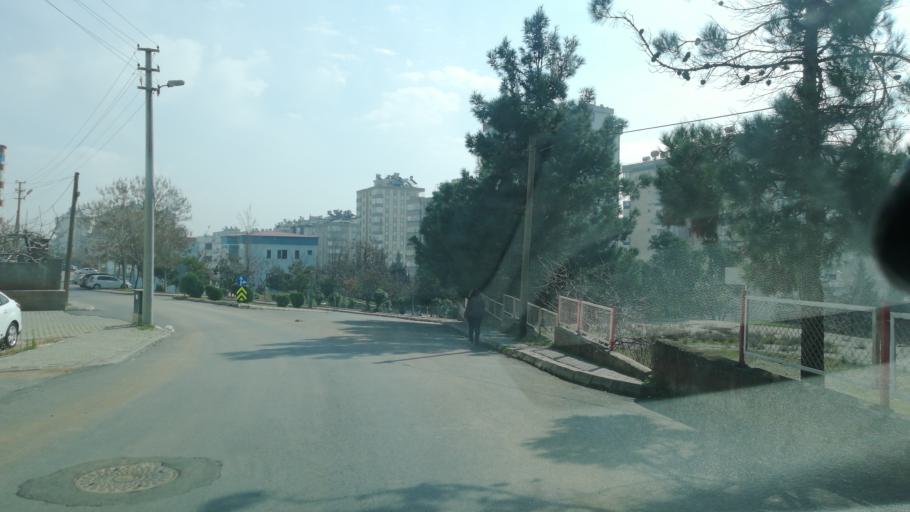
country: TR
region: Kahramanmaras
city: Kahramanmaras
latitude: 37.5894
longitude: 36.8883
